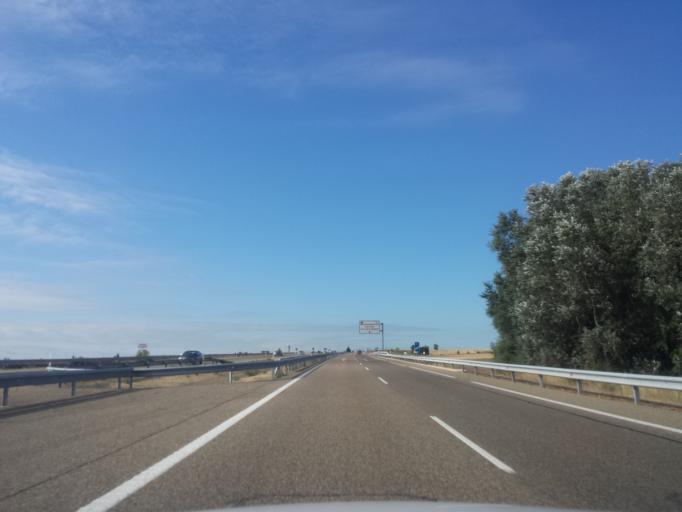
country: ES
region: Castille and Leon
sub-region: Provincia de Leon
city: Ardon
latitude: 42.4450
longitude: -5.5823
